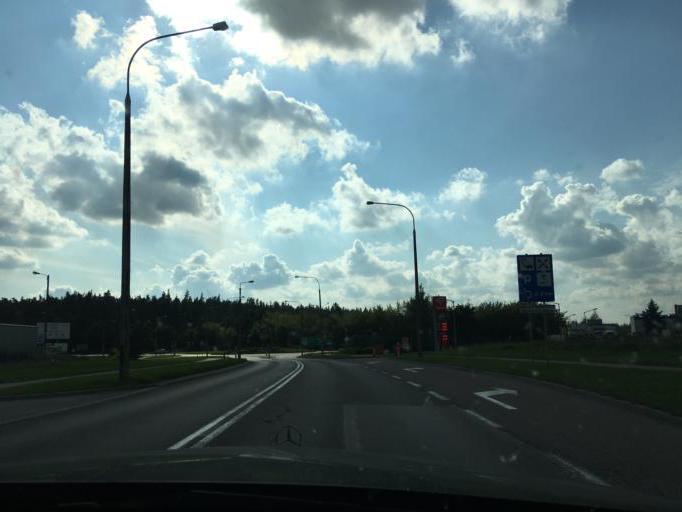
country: PL
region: Podlasie
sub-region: Suwalki
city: Suwalki
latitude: 54.0718
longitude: 22.9353
